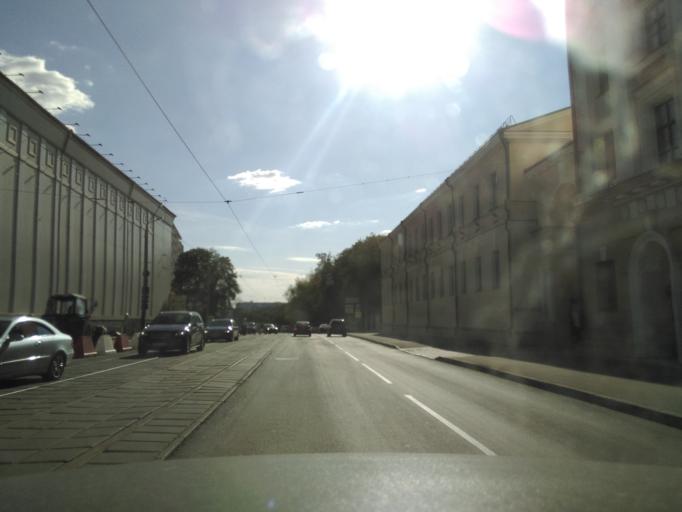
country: BY
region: Minsk
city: Minsk
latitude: 53.9027
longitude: 27.5793
